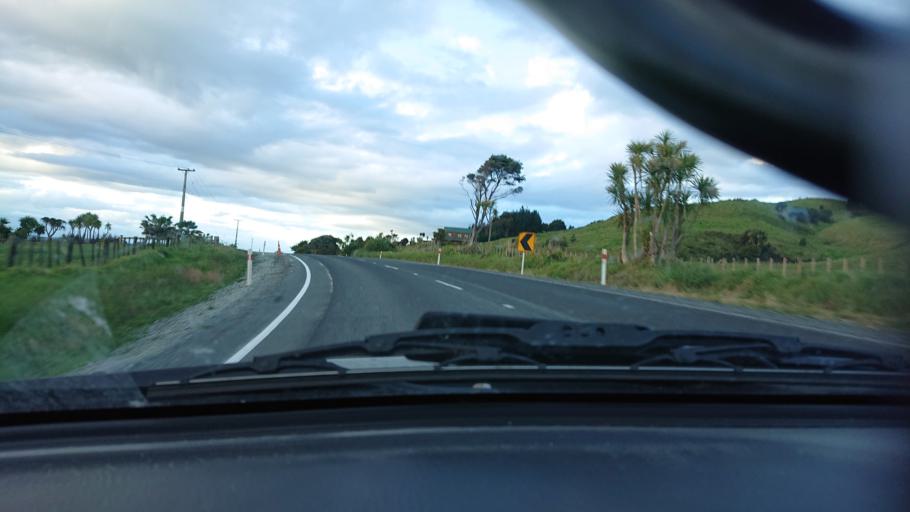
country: NZ
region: Auckland
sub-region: Auckland
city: Wellsford
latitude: -36.4477
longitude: 174.4336
